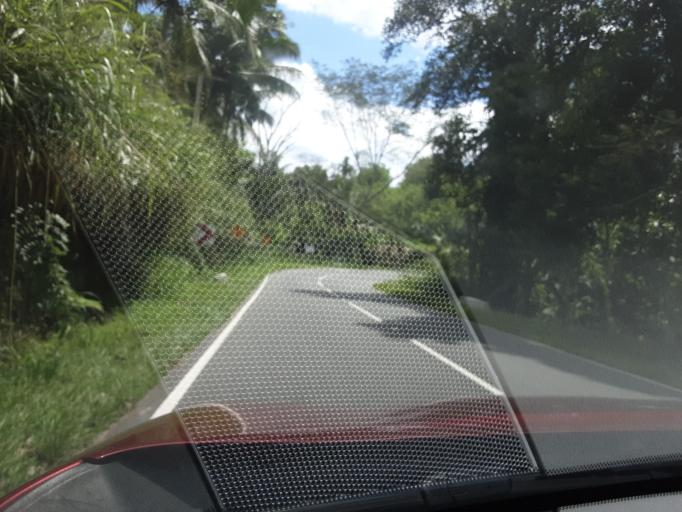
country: LK
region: Uva
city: Monaragala
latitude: 6.8974
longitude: 81.2748
